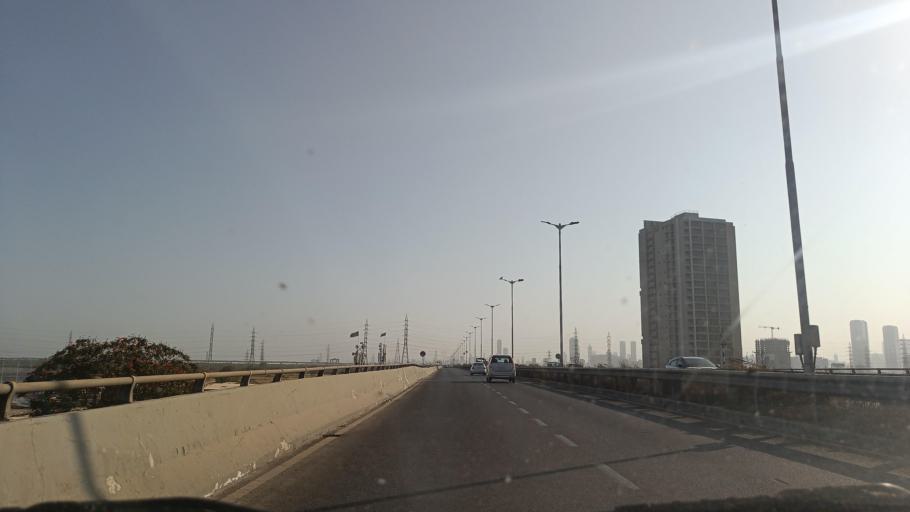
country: IN
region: Maharashtra
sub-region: Mumbai Suburban
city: Mumbai
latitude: 19.0220
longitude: 72.8761
